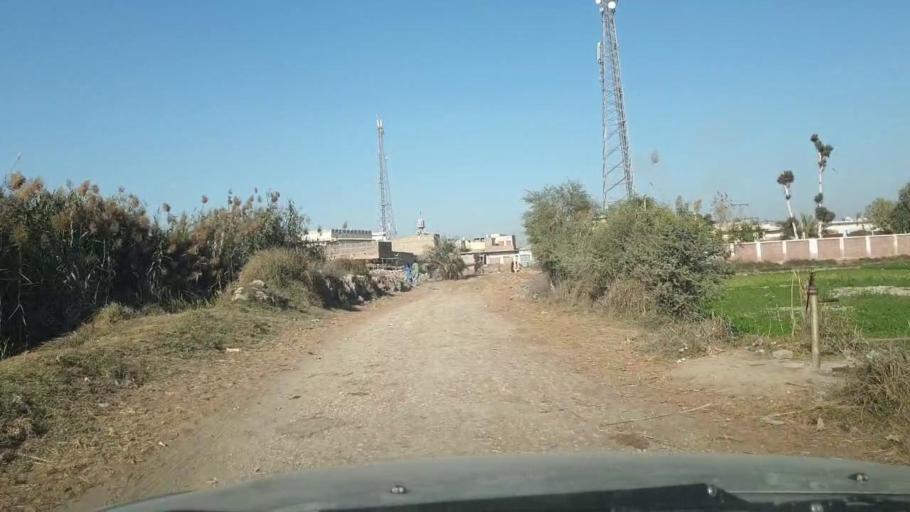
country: PK
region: Sindh
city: Ghotki
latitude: 28.0605
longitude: 69.3379
